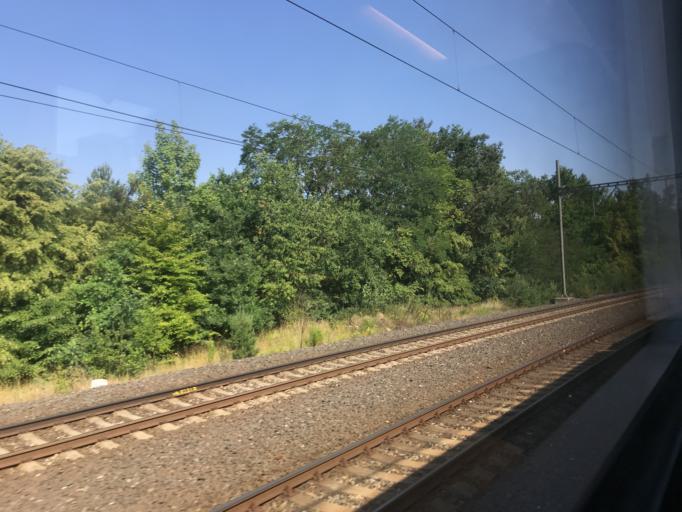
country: CZ
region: Central Bohemia
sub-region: Okres Praha-Vychod
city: Mnichovice
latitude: 49.8989
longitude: 14.7271
